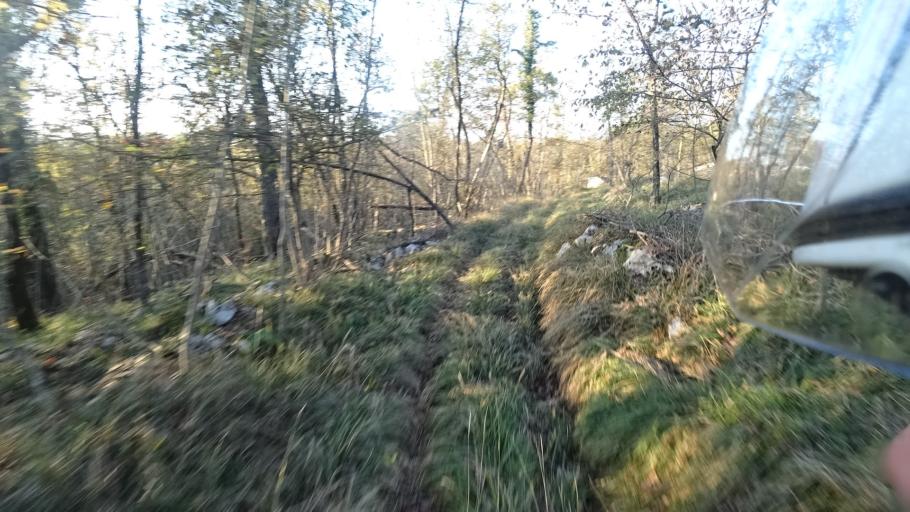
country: HR
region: Primorsko-Goranska
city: Kastav
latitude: 45.4100
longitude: 14.3165
